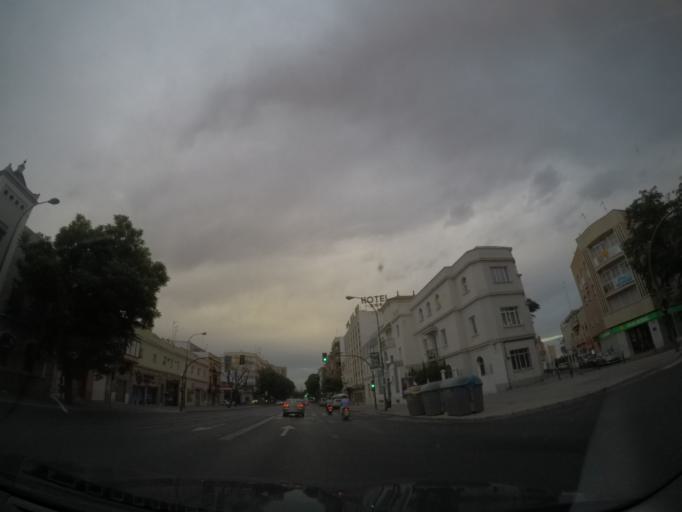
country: ES
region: Andalusia
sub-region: Provincia de Sevilla
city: Sevilla
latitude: 37.3874
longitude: -5.9676
